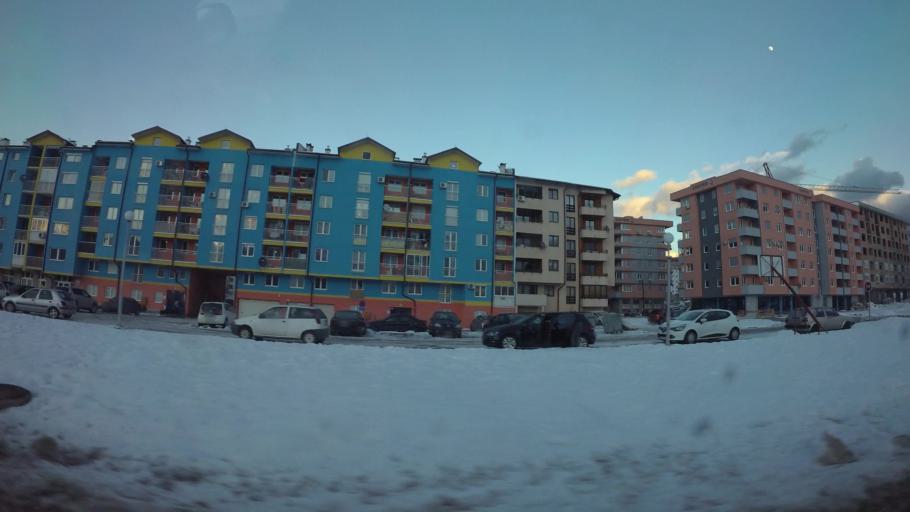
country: BA
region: Federation of Bosnia and Herzegovina
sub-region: Kanton Sarajevo
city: Sarajevo
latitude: 43.8167
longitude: 18.3606
